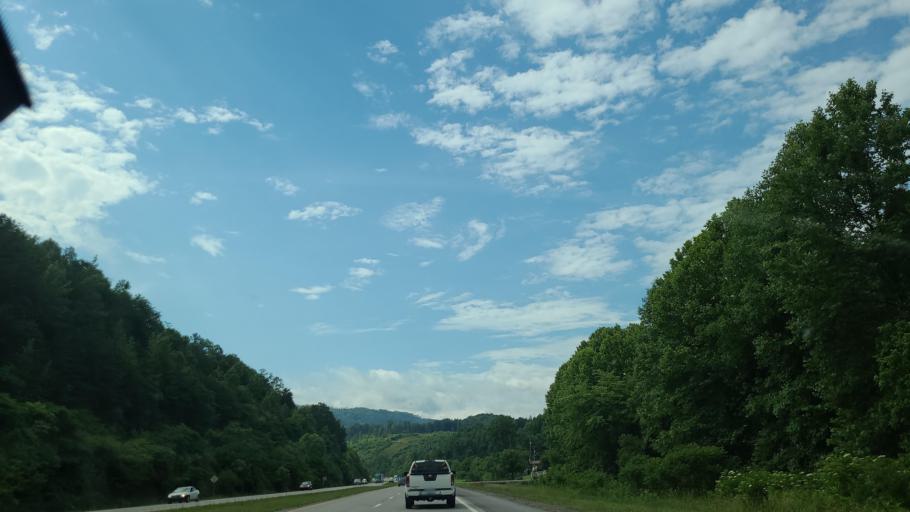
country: US
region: Kentucky
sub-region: Bell County
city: Pineville
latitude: 36.7040
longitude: -83.6957
